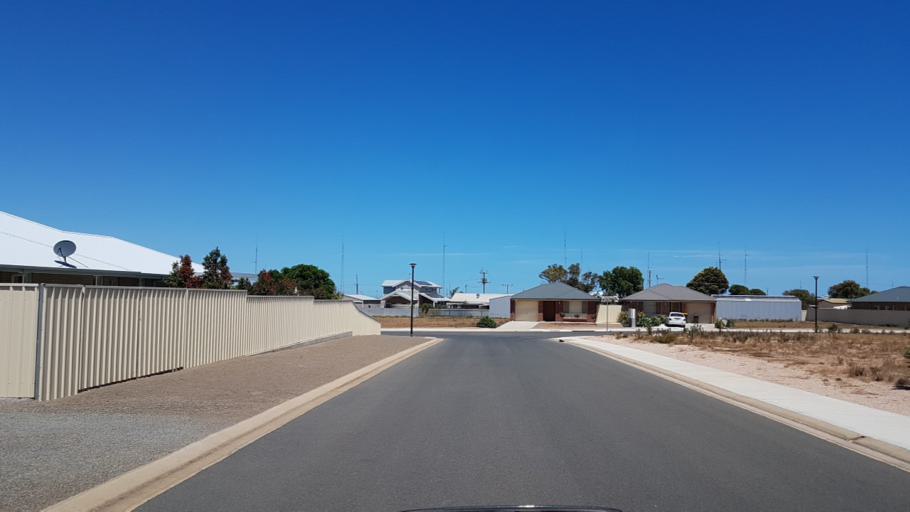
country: AU
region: South Australia
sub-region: Copper Coast
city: Wallaroo
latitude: -33.8933
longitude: 137.6299
